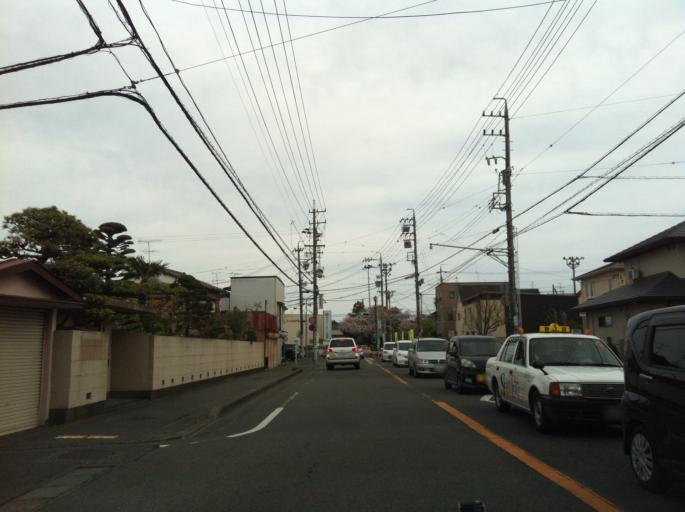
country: JP
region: Shizuoka
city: Shizuoka-shi
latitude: 35.0002
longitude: 138.4711
